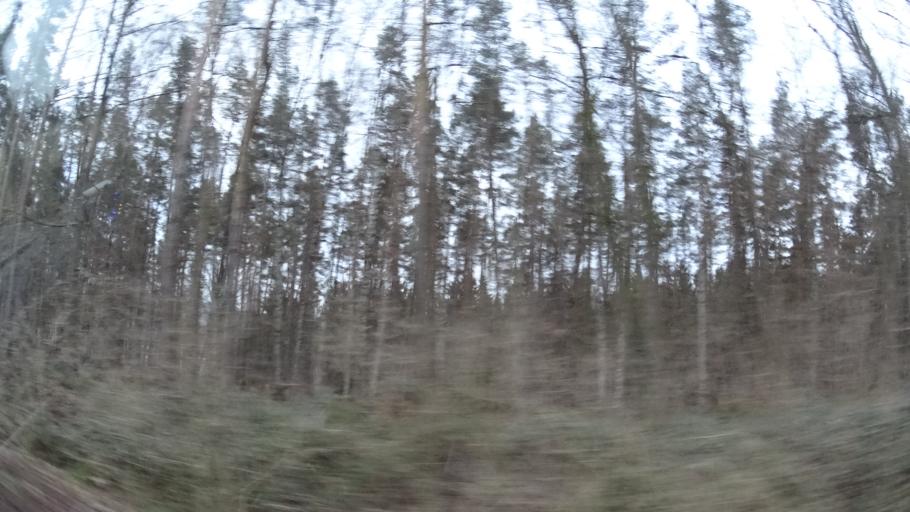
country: DE
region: Thuringia
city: Neustadt (Orla)
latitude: 50.7496
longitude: 11.7222
